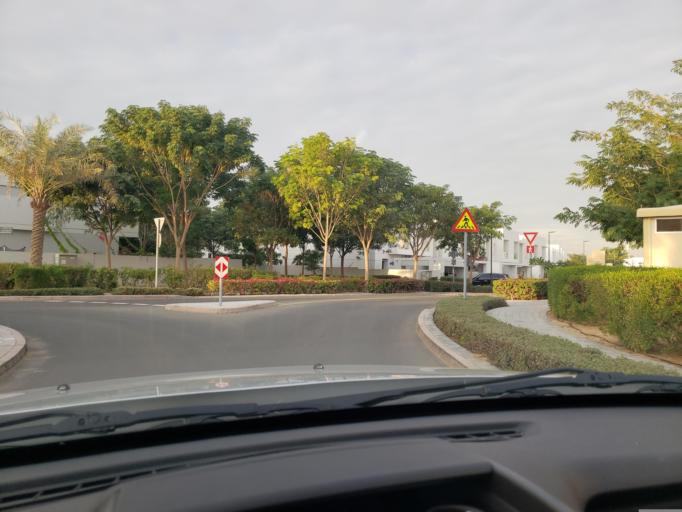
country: AE
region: Dubai
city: Dubai
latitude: 25.0145
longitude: 55.2687
